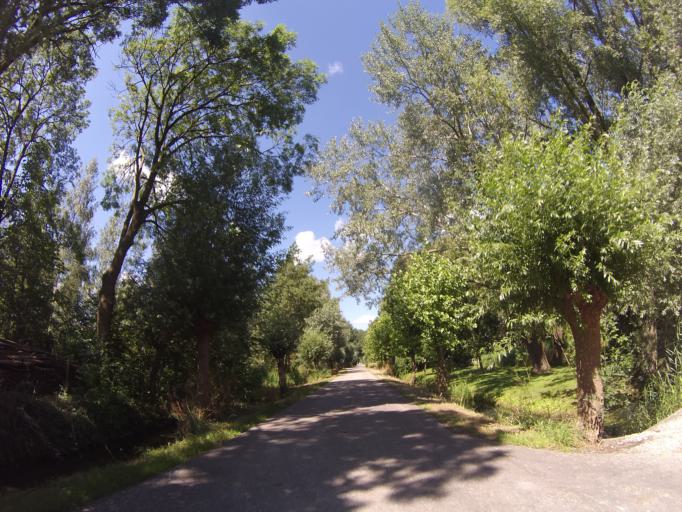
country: NL
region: Utrecht
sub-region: Stichtse Vecht
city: Spechtenkamp
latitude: 52.1124
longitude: 5.0207
